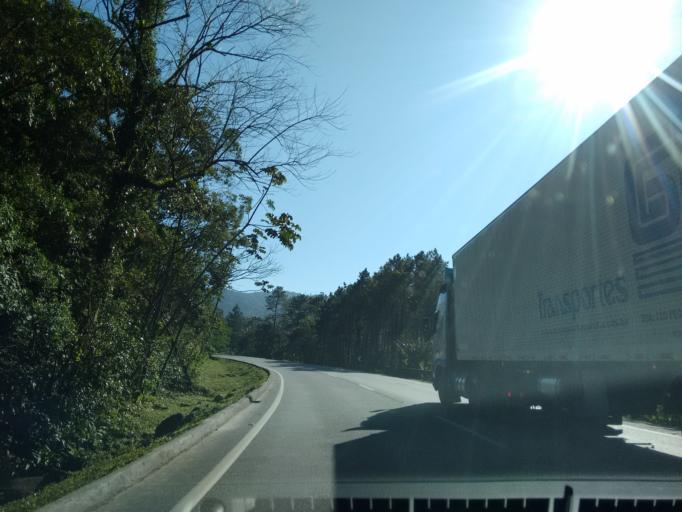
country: BR
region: Parana
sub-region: Guaratuba
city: Guaratuba
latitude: -25.9128
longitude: -48.9192
